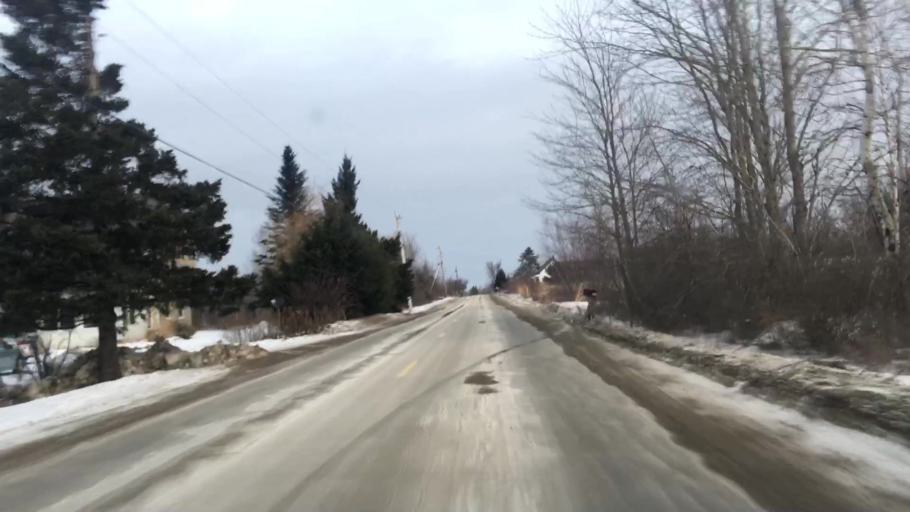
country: US
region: Maine
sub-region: Hancock County
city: Franklin
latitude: 44.7303
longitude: -68.3354
